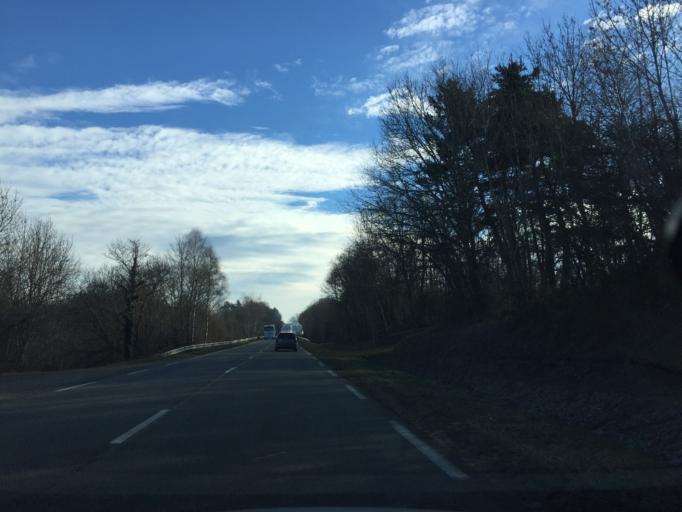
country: FR
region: Auvergne
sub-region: Departement du Puy-de-Dome
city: Gelles
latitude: 45.8527
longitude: 2.6921
